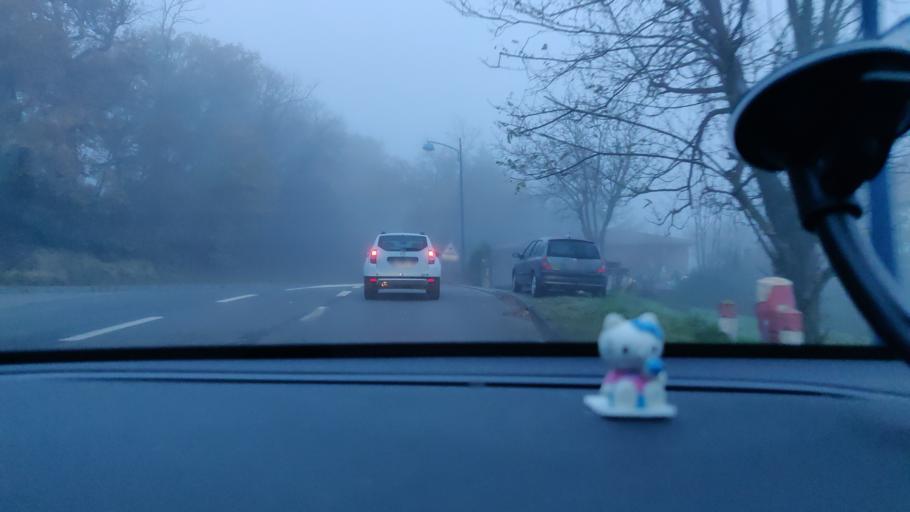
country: FR
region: Midi-Pyrenees
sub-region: Departement de la Haute-Garonne
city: Vieille-Toulouse
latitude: 43.5246
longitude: 1.4622
